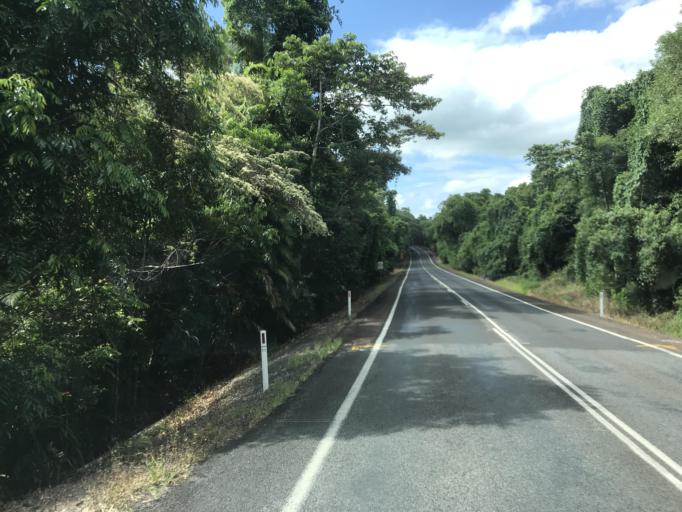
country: AU
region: Queensland
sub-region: Cassowary Coast
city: Innisfail
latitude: -17.8537
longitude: 146.0663
